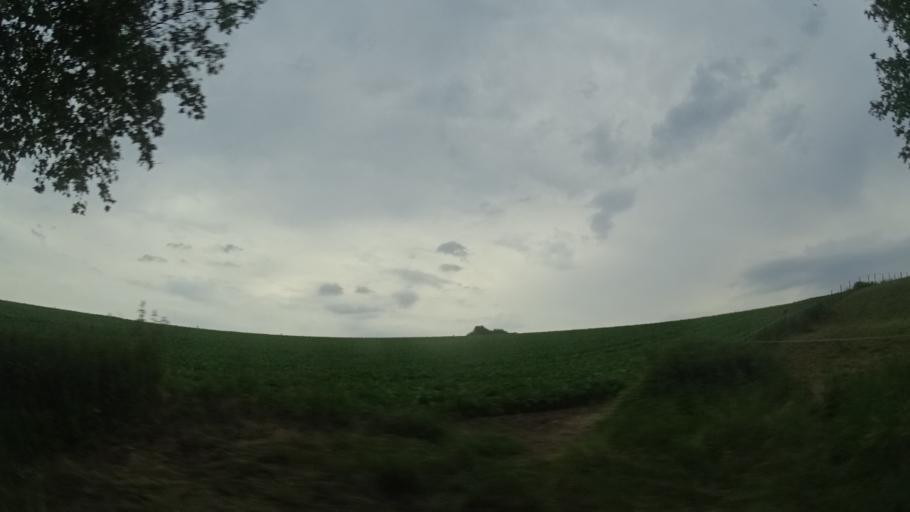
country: DE
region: Lower Saxony
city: Halle
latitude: 52.0012
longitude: 9.5537
